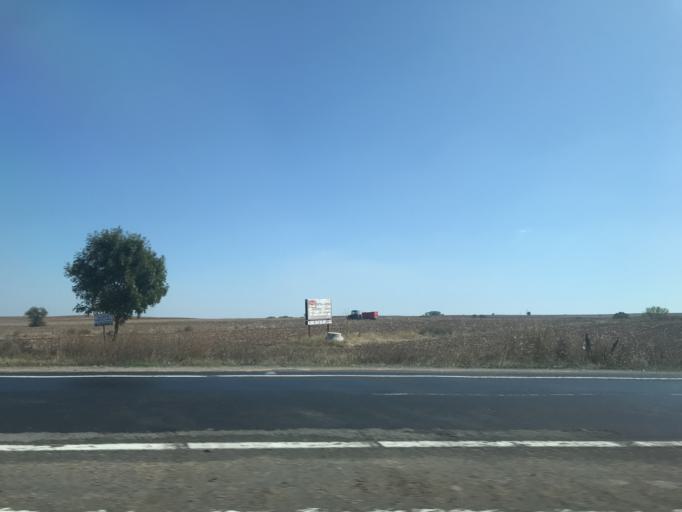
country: TR
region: Tekirdag
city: Muratli
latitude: 41.1400
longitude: 27.4934
